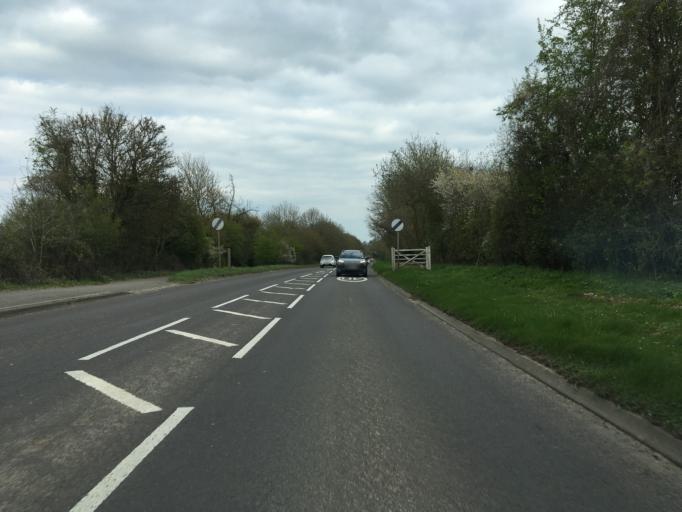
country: GB
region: England
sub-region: Oxfordshire
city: Witney
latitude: 51.7965
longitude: -1.5417
